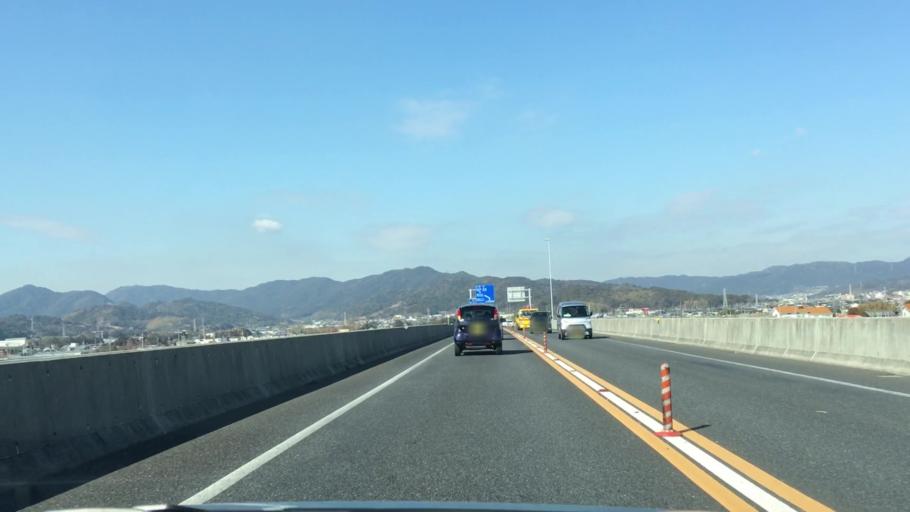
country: JP
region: Aichi
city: Kozakai-cho
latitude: 34.8125
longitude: 137.3339
